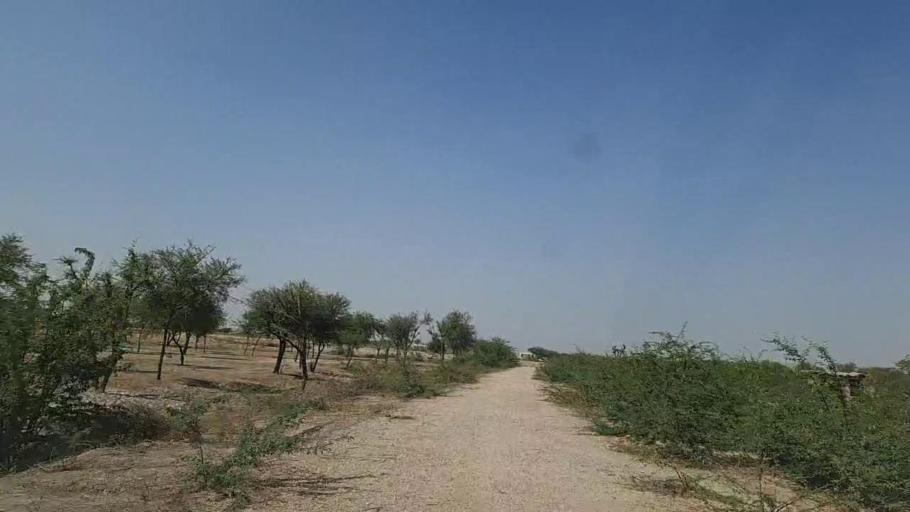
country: PK
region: Sindh
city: Naukot
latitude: 24.6334
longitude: 69.2926
